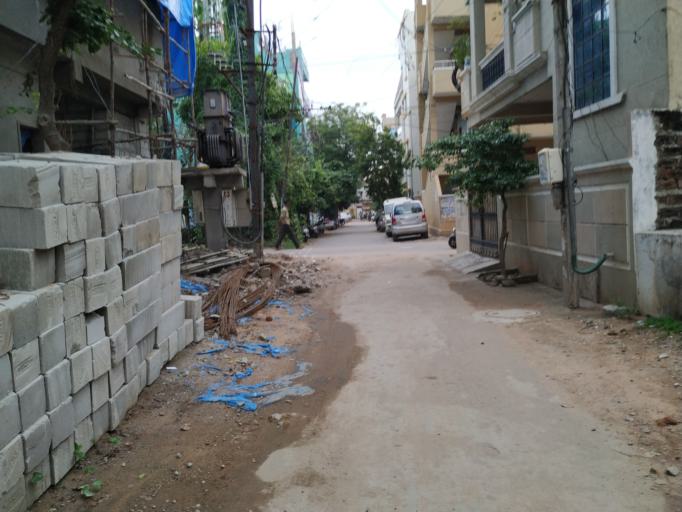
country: IN
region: Telangana
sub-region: Rangareddi
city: Quthbullapur
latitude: 17.4669
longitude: 78.4575
